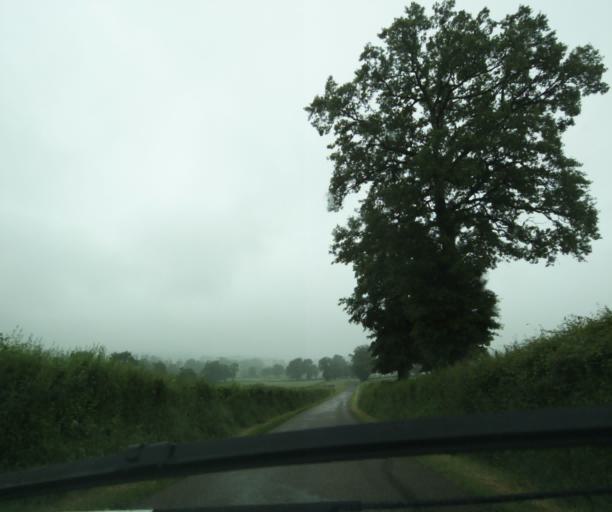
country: FR
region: Bourgogne
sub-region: Departement de Saone-et-Loire
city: Charolles
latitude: 46.4109
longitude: 4.2854
